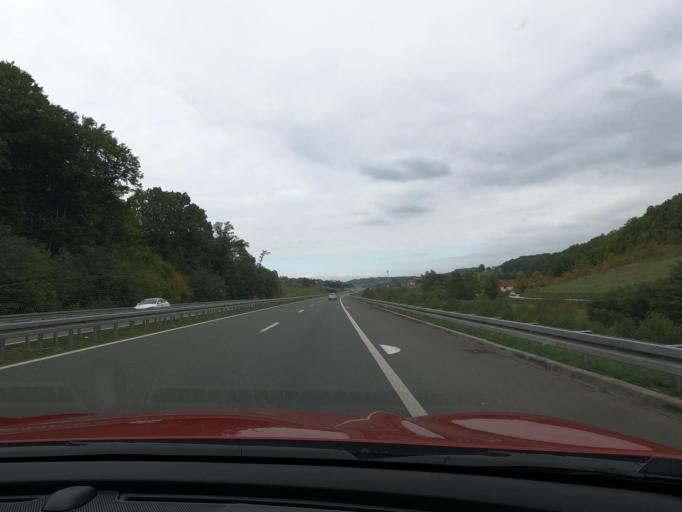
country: RS
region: Central Serbia
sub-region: Moravicki Okrug
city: Gornji Milanovac
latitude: 44.0640
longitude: 20.3801
